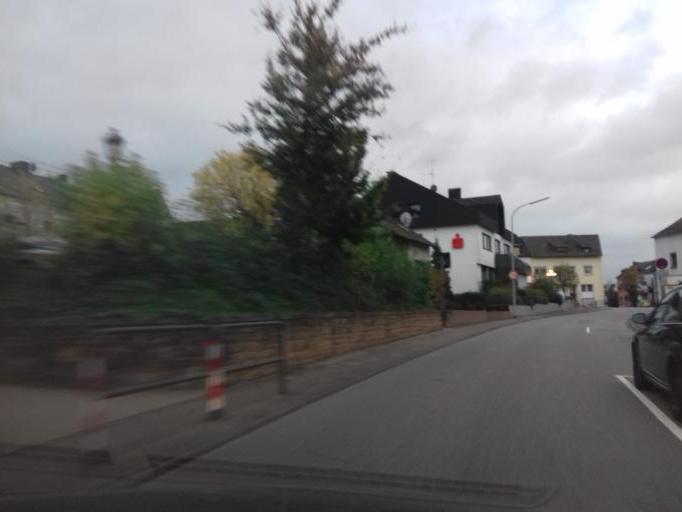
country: DE
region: Rheinland-Pfalz
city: Tawern
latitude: 49.6722
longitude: 6.5212
